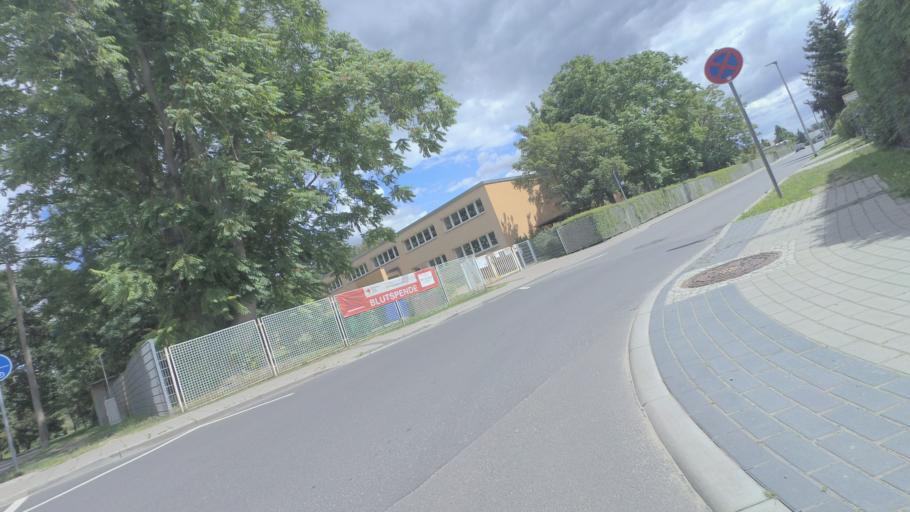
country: DE
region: Brandenburg
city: Luckenwalde
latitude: 52.1003
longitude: 13.1527
